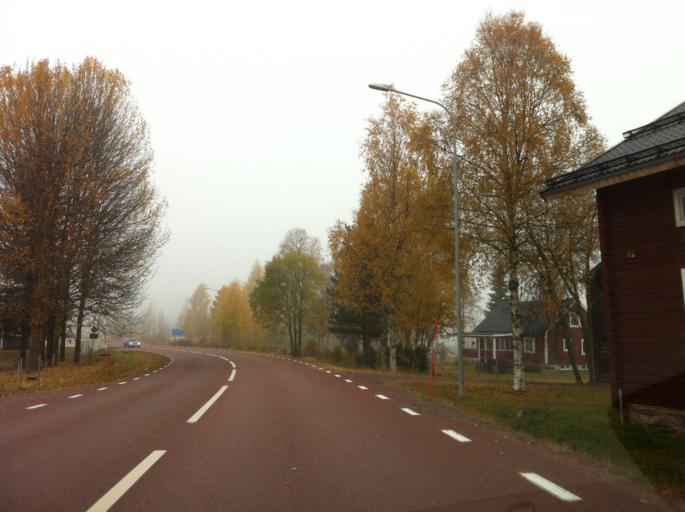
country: NO
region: Hedmark
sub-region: Trysil
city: Innbygda
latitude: 61.6879
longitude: 13.1629
